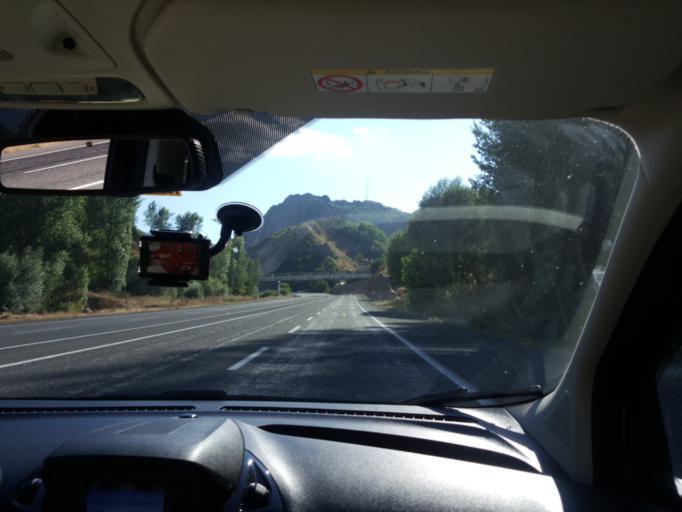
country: TR
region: Sivas
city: Aksu
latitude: 40.0494
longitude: 38.0487
